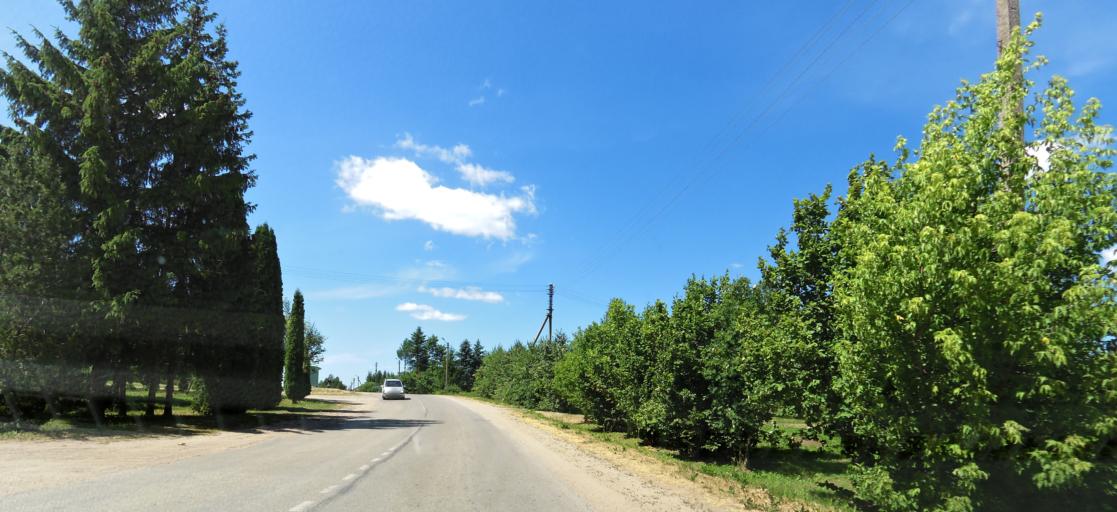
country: LT
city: Vabalninkas
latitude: 55.9421
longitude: 24.8792
